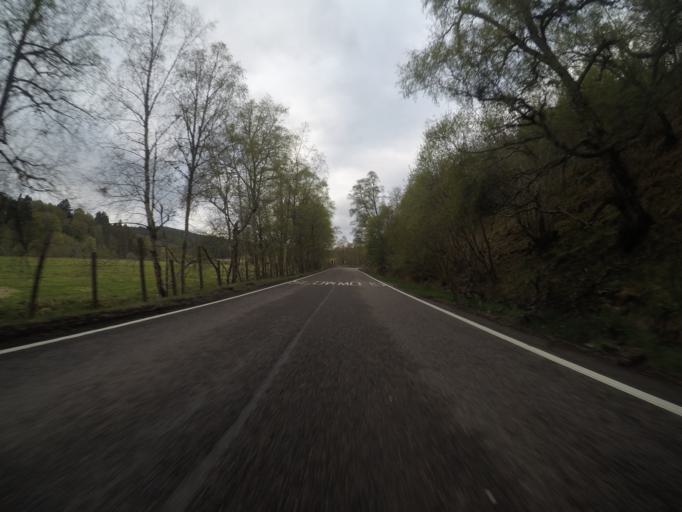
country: GB
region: Scotland
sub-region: Highland
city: Kingussie
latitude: 56.9752
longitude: -4.3822
